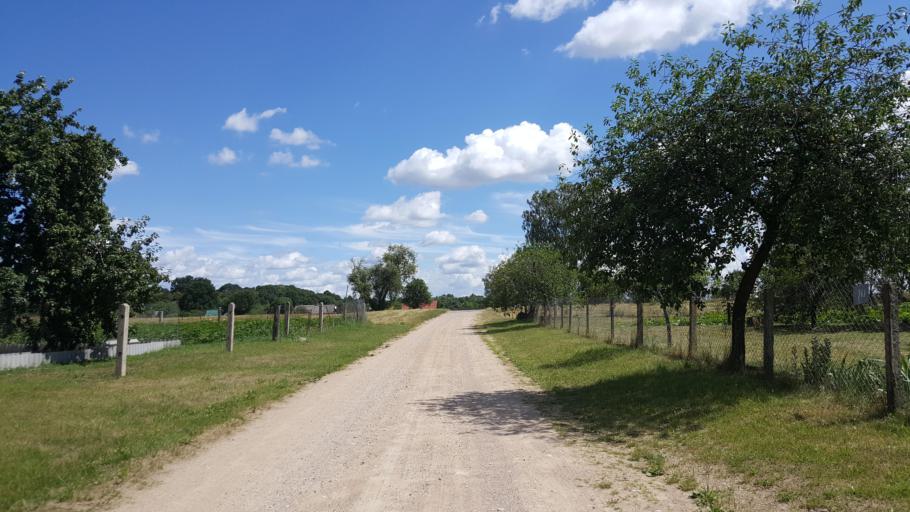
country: BY
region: Brest
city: Kamyanyets
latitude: 52.3107
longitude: 23.9199
